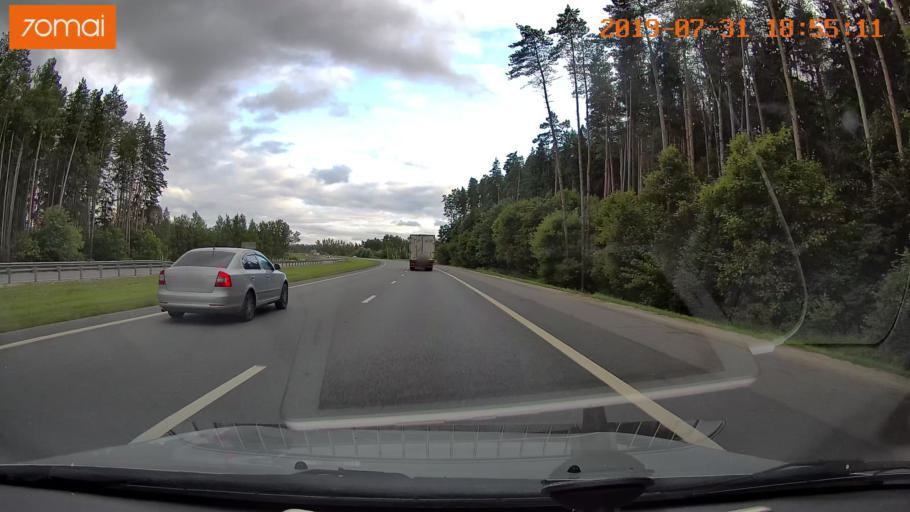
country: RU
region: Moskovskaya
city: Raduzhnyy
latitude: 55.1790
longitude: 38.6676
